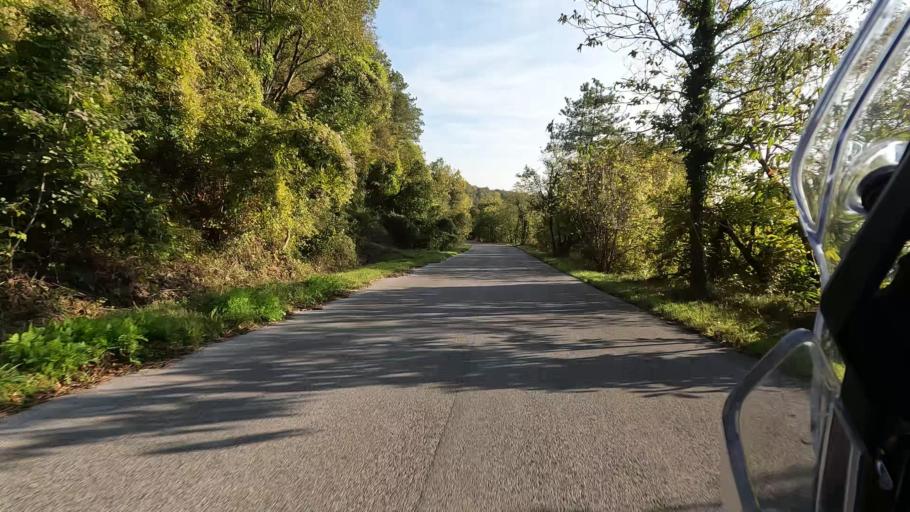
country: IT
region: Liguria
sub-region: Provincia di Savona
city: San Giovanni
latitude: 44.4146
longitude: 8.5285
